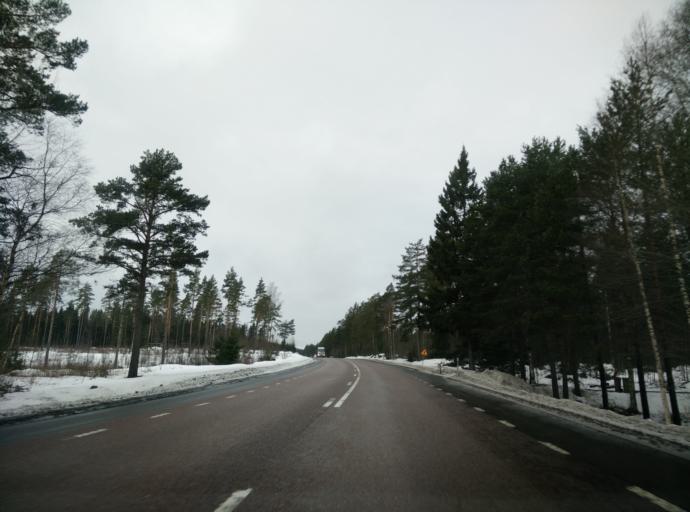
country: SE
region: Gaevleborg
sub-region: Hofors Kommun
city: Hofors
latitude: 60.5639
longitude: 16.3633
